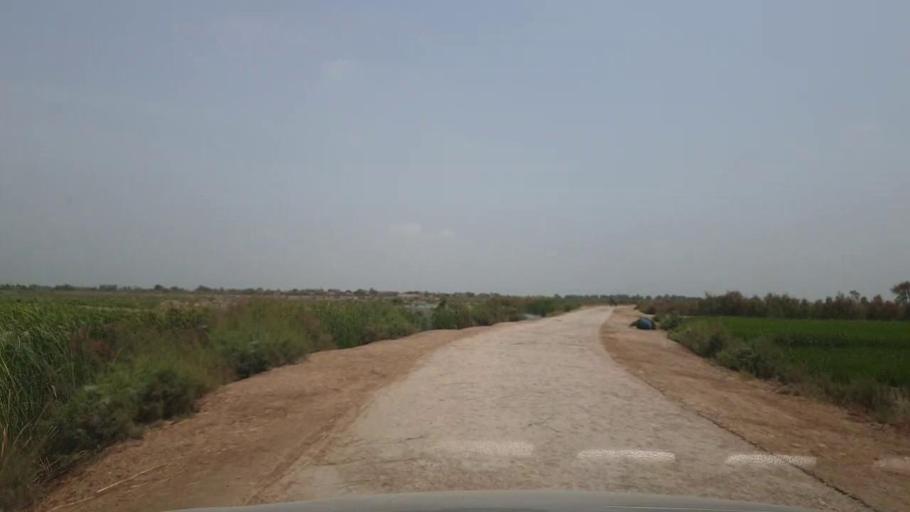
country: PK
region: Sindh
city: Garhi Yasin
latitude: 27.9413
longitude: 68.3827
